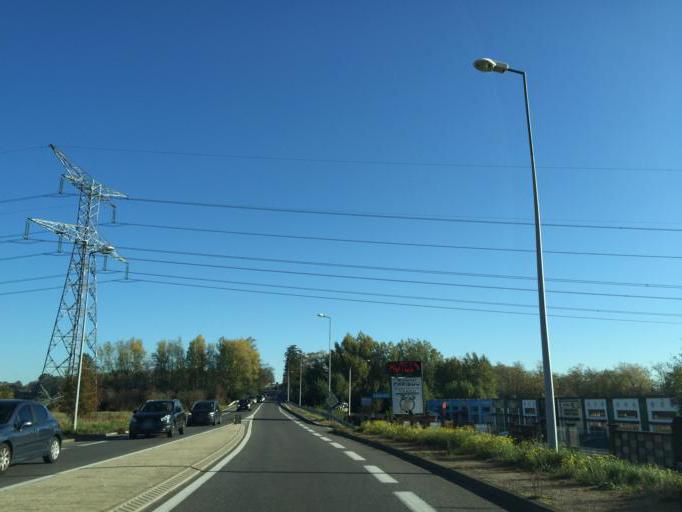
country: FR
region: Rhone-Alpes
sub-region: Departement du Rhone
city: Taluyers
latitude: 45.6190
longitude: 4.7106
